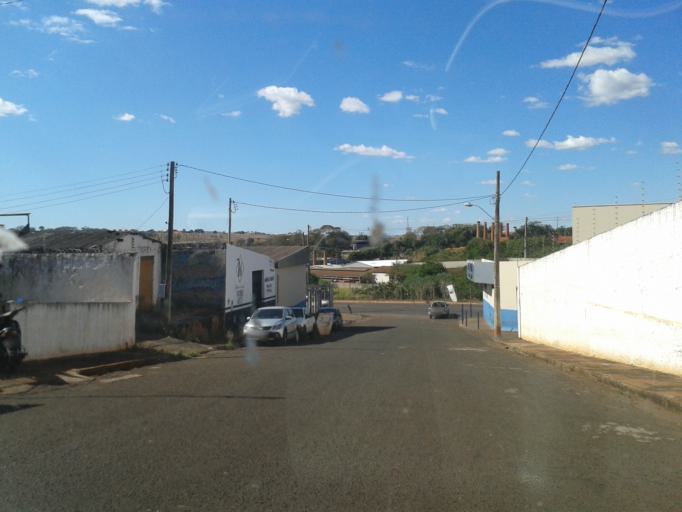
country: BR
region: Minas Gerais
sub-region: Ituiutaba
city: Ituiutaba
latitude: -18.9540
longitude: -49.4574
